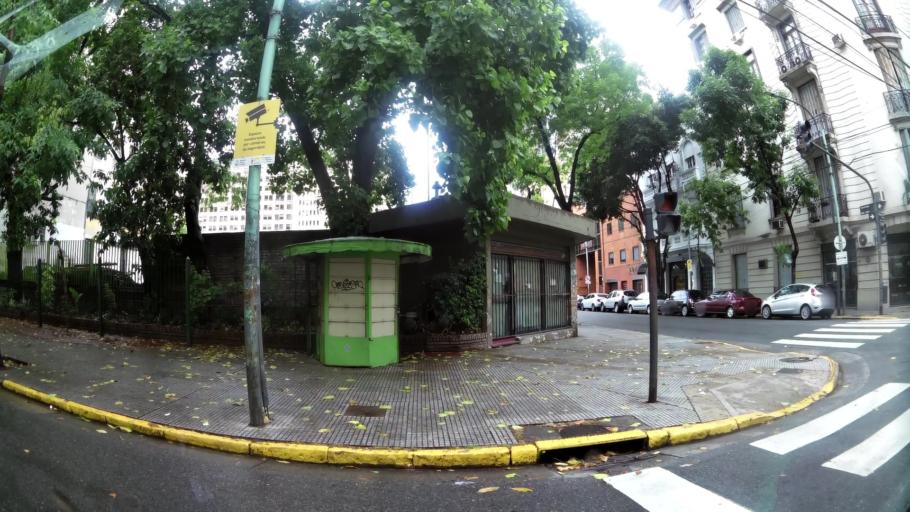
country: AR
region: Buenos Aires F.D.
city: Retiro
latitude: -34.5968
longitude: -58.4003
